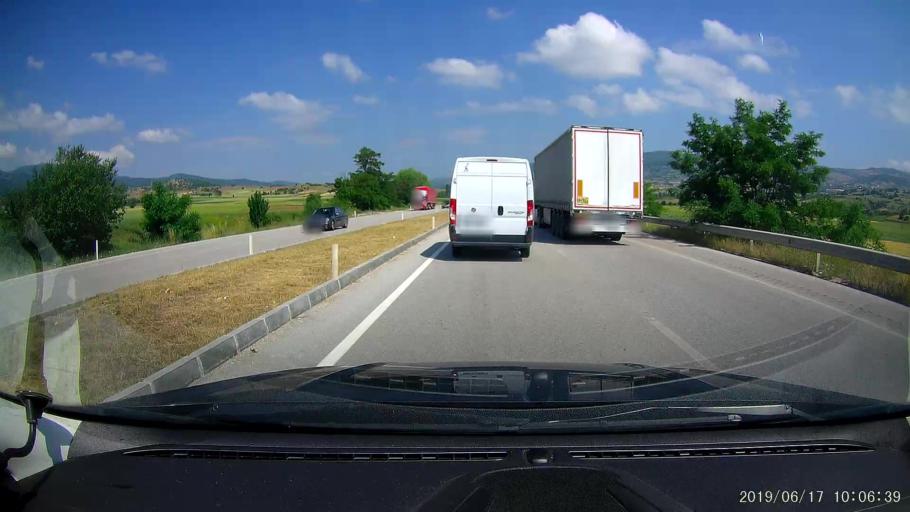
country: TR
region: Amasya
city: Gumushacikoy
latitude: 40.9083
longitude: 35.1765
